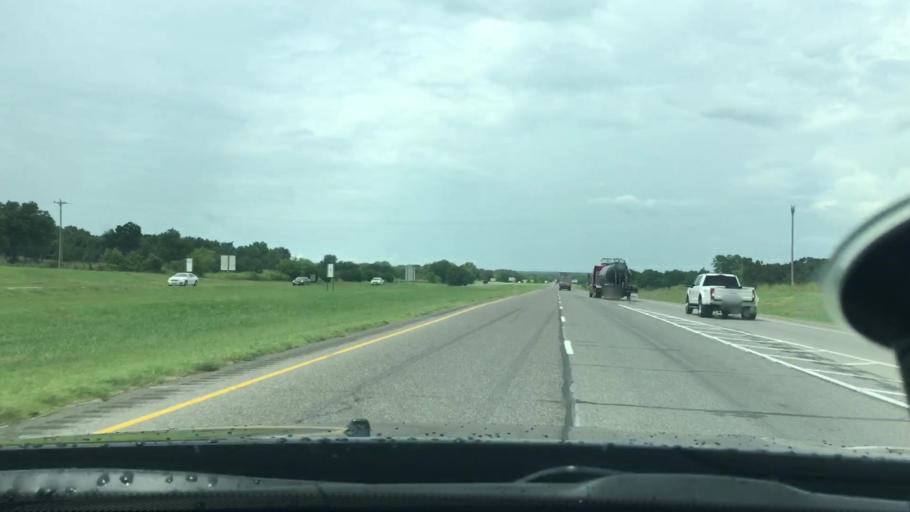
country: US
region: Oklahoma
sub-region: Murray County
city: Davis
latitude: 34.5087
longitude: -97.1756
